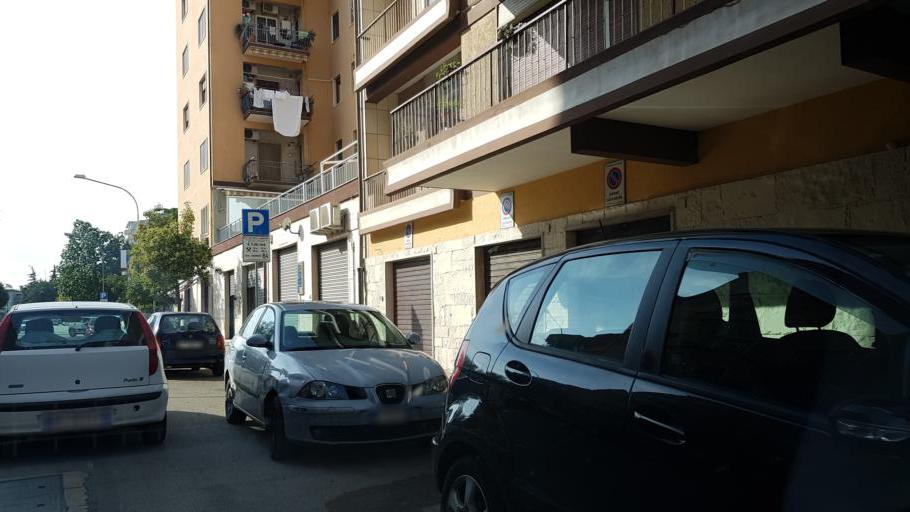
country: IT
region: Apulia
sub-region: Provincia di Foggia
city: Foggia
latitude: 41.4543
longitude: 15.5617
